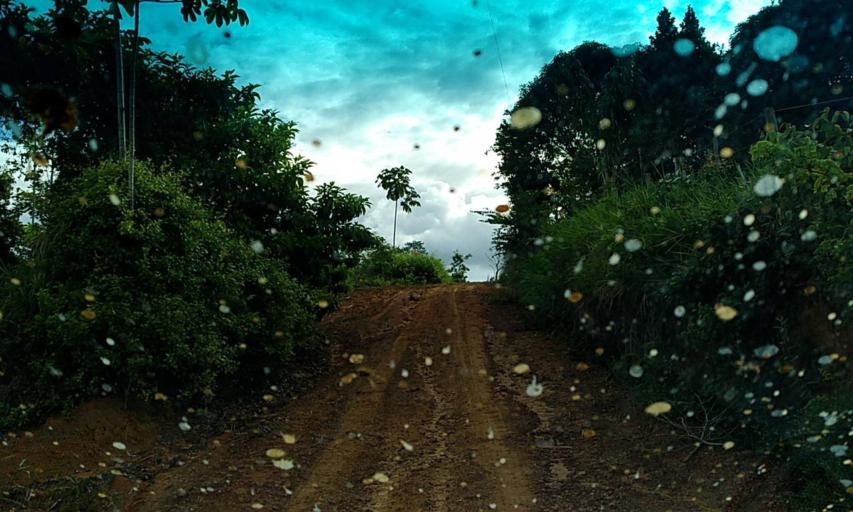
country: BR
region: Para
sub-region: Senador Jose Porfirio
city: Senador Jose Porfirio
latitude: -3.0043
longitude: -51.7408
